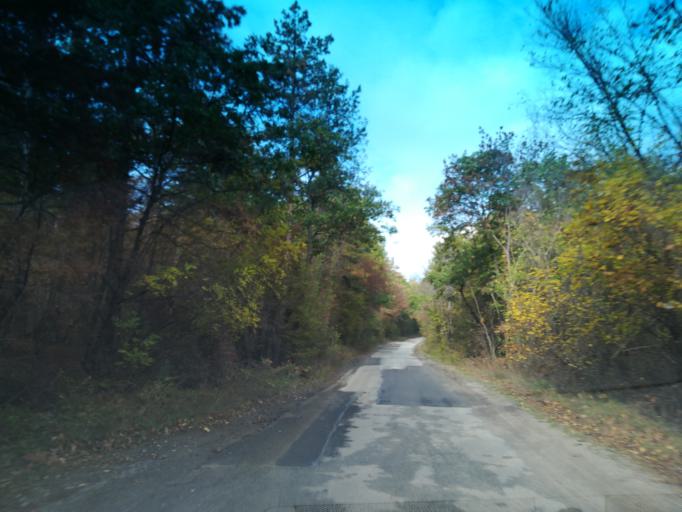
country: BG
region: Stara Zagora
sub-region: Obshtina Nikolaevo
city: Elkhovo
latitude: 42.3197
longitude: 25.4033
